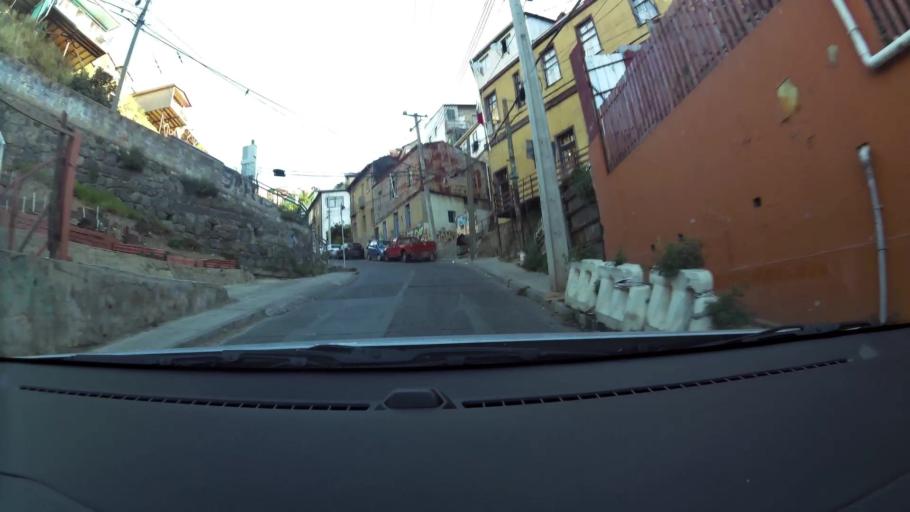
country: CL
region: Valparaiso
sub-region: Provincia de Valparaiso
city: Valparaiso
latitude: -33.0539
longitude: -71.6111
